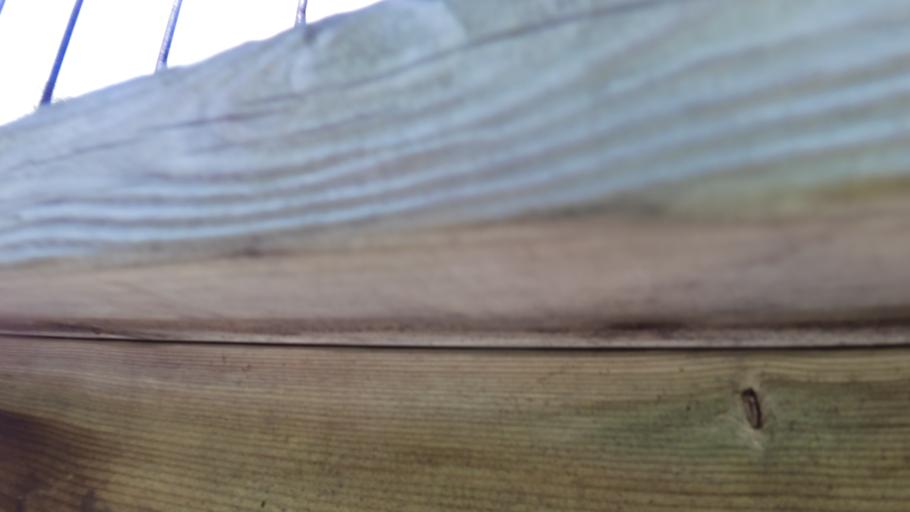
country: CA
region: Ontario
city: Temiskaming Shores
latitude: 47.3858
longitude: -79.6873
